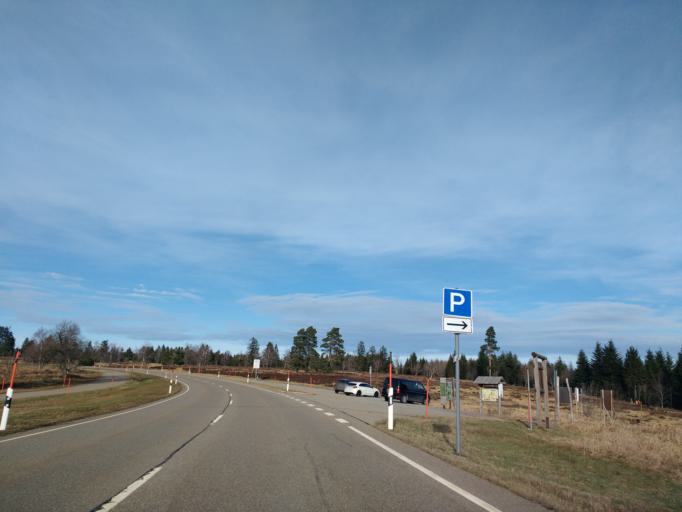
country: DE
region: Baden-Wuerttemberg
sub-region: Freiburg Region
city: Bad Peterstal-Griesbach
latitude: 48.4913
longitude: 8.2687
